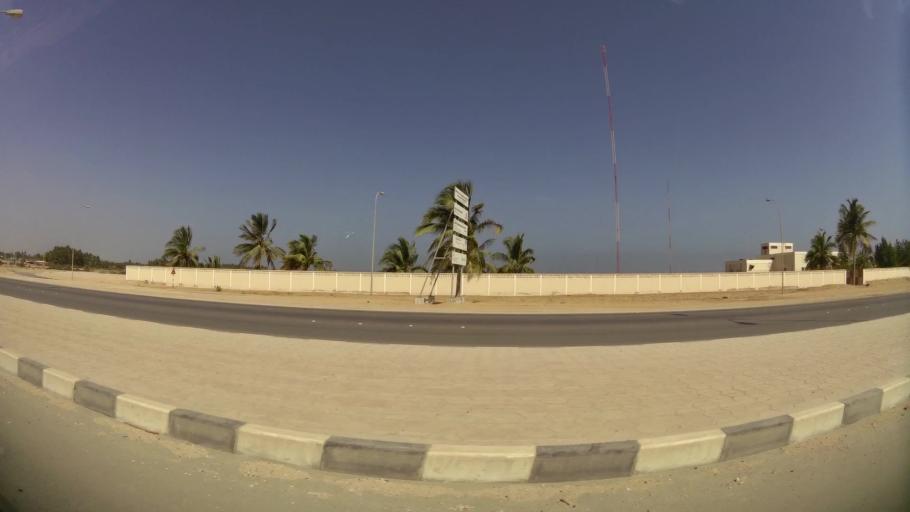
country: OM
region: Zufar
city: Salalah
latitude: 16.9946
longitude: 54.0300
